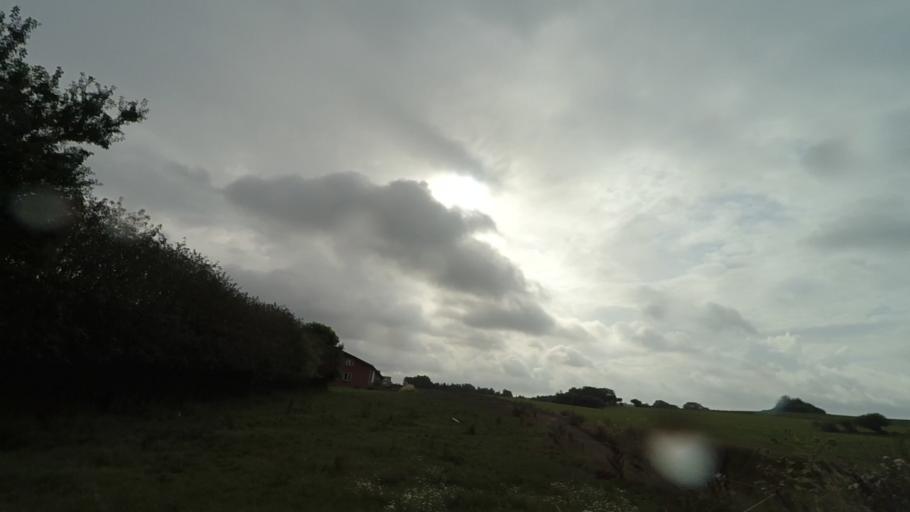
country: DK
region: Central Jutland
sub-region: Syddjurs Kommune
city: Ronde
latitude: 56.2997
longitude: 10.4449
